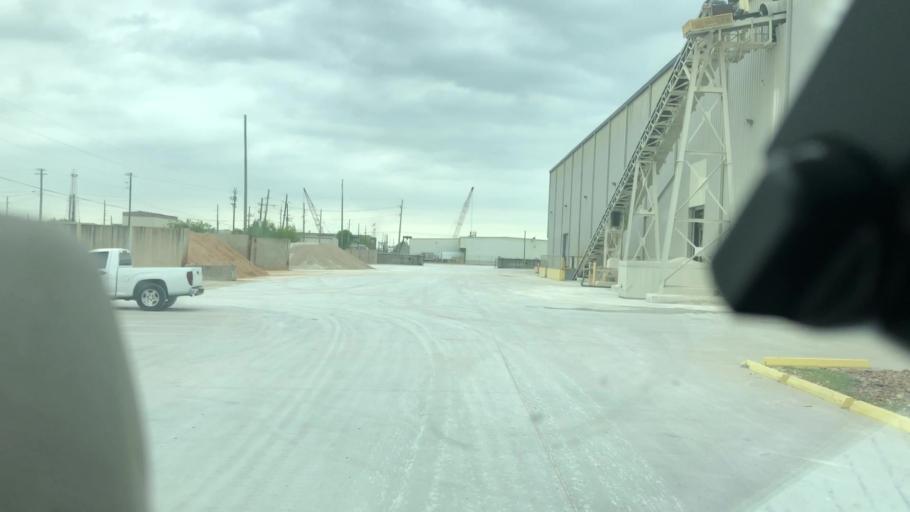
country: US
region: Texas
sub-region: Harris County
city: Jersey Village
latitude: 29.8740
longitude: -95.5800
